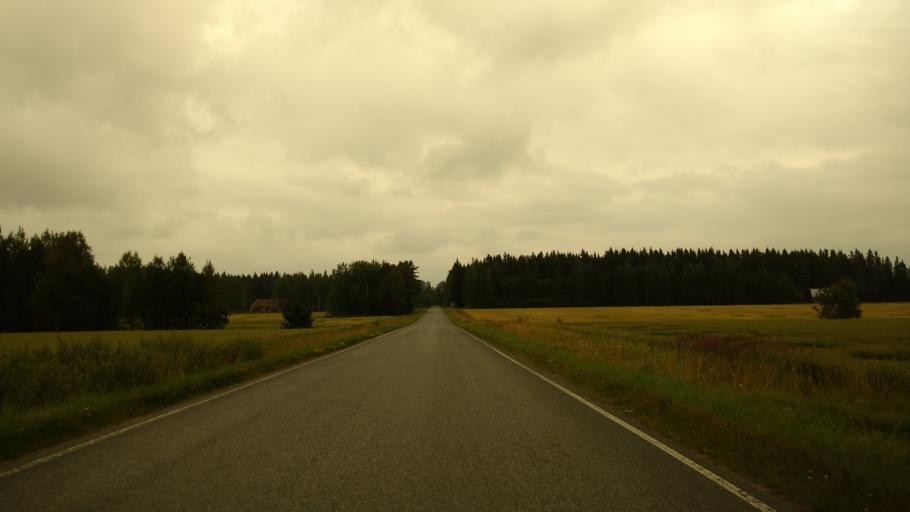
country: FI
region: Haeme
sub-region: Forssa
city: Ypaejae
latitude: 60.7554
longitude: 23.2083
